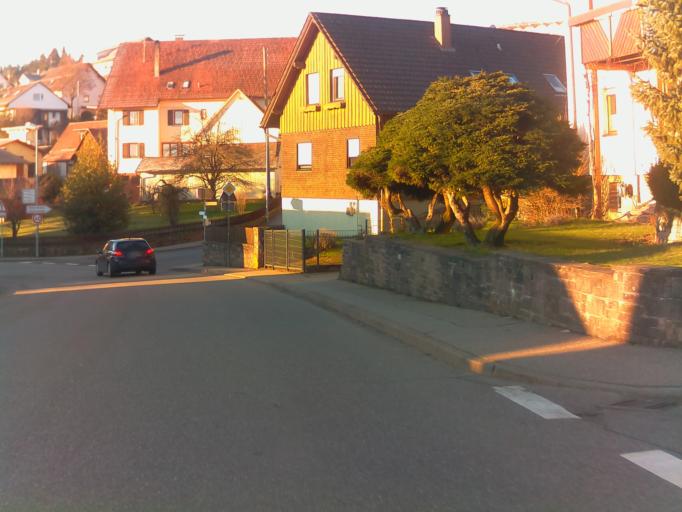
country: DE
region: Baden-Wuerttemberg
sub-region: Karlsruhe Region
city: Schomberg
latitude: 48.7881
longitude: 8.6417
